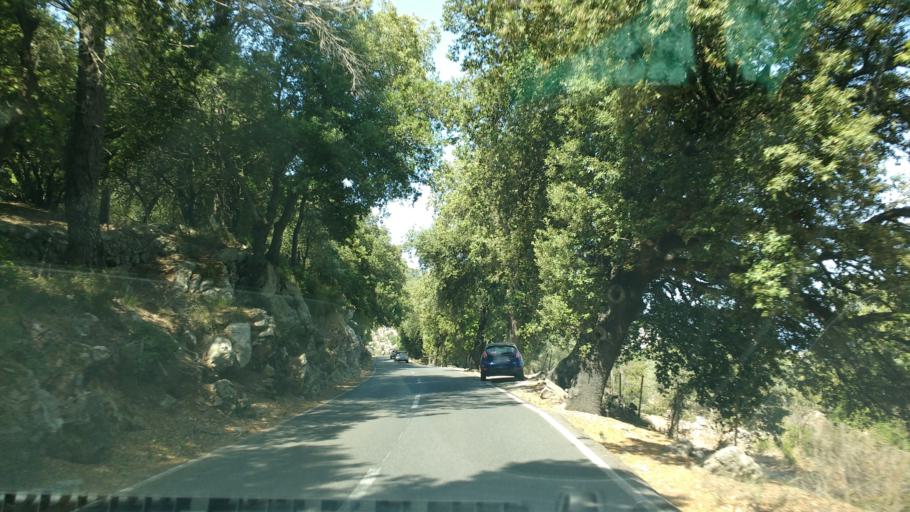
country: ES
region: Balearic Islands
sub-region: Illes Balears
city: Escorca
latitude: 39.8265
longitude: 2.8442
